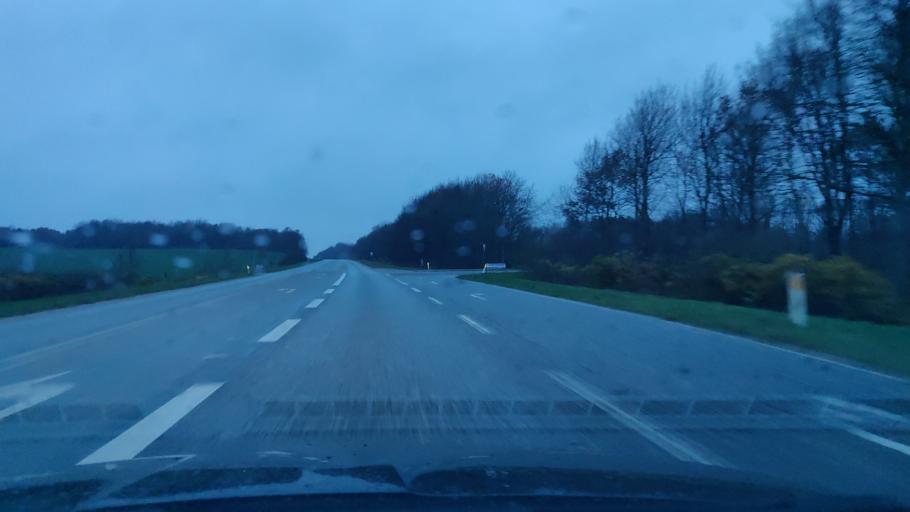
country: DK
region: Central Jutland
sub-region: Herning Kommune
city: Avlum
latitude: 56.2821
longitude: 8.7500
